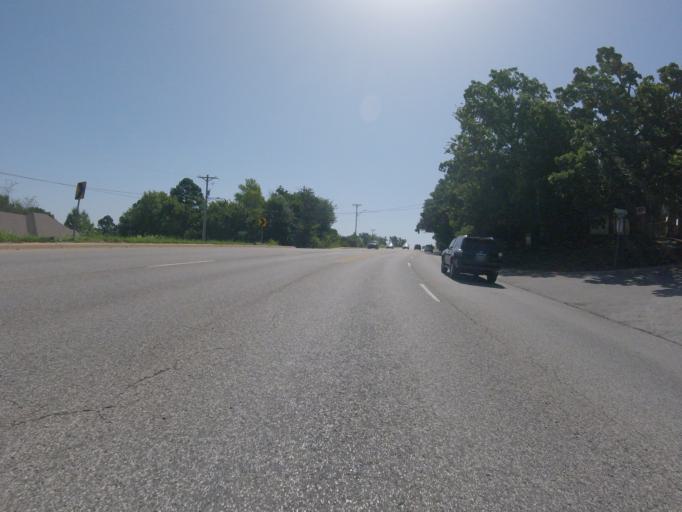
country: US
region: Arkansas
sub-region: Washington County
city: Fayetteville
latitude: 36.0792
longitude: -94.1812
